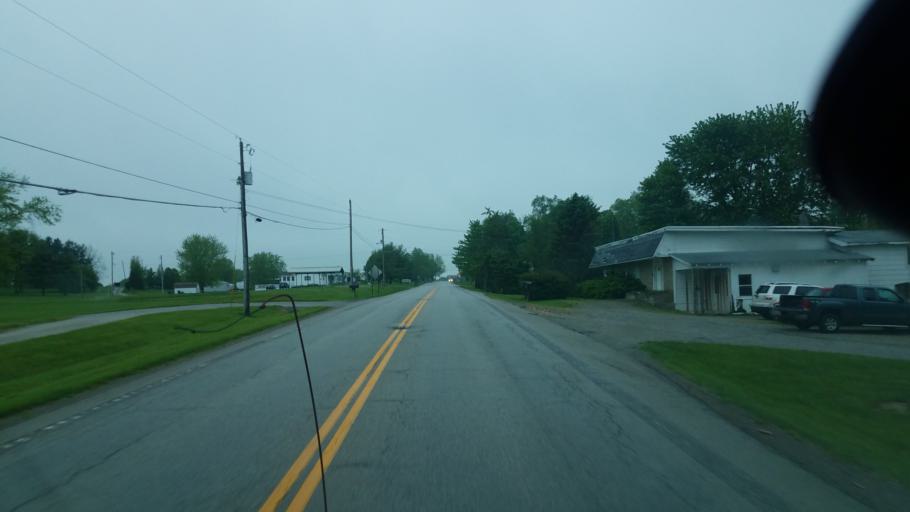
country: US
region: Ohio
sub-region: Highland County
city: Hillsboro
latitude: 39.2658
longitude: -83.5984
